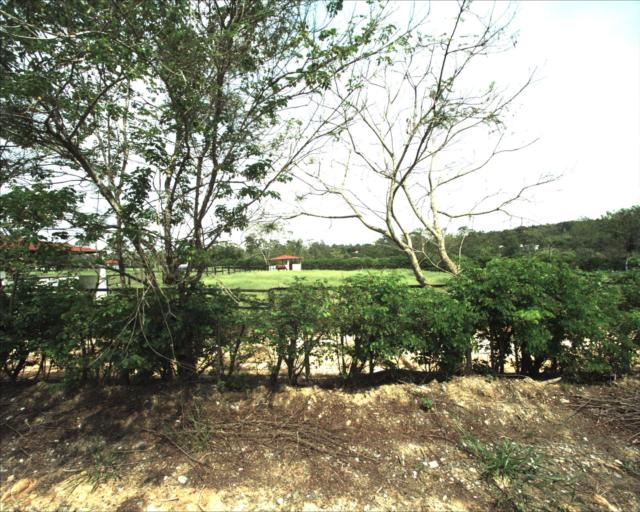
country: BR
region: Sao Paulo
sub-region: Aracoiaba Da Serra
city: Aracoiaba da Serra
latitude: -23.5586
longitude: -47.5366
